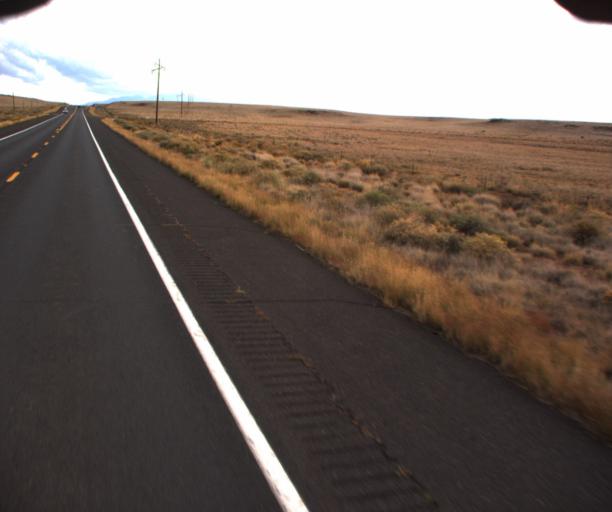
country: US
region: Arizona
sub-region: Coconino County
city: Flagstaff
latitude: 35.6615
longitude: -111.5129
